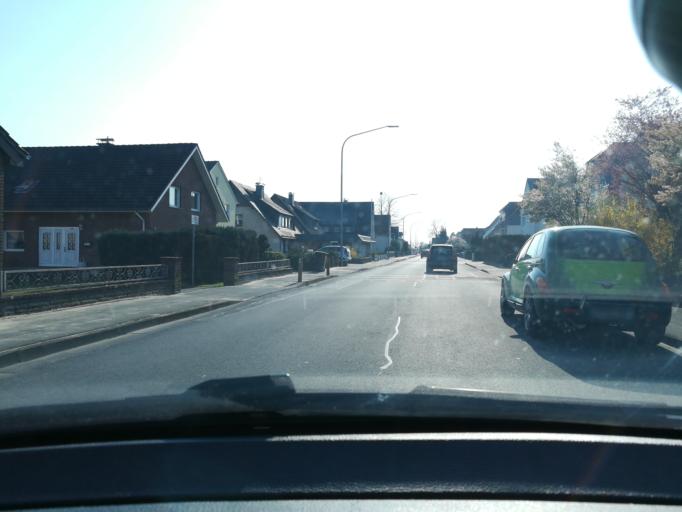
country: DE
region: North Rhine-Westphalia
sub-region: Regierungsbezirk Detmold
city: Oerlinghausen
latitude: 51.9307
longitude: 8.6071
